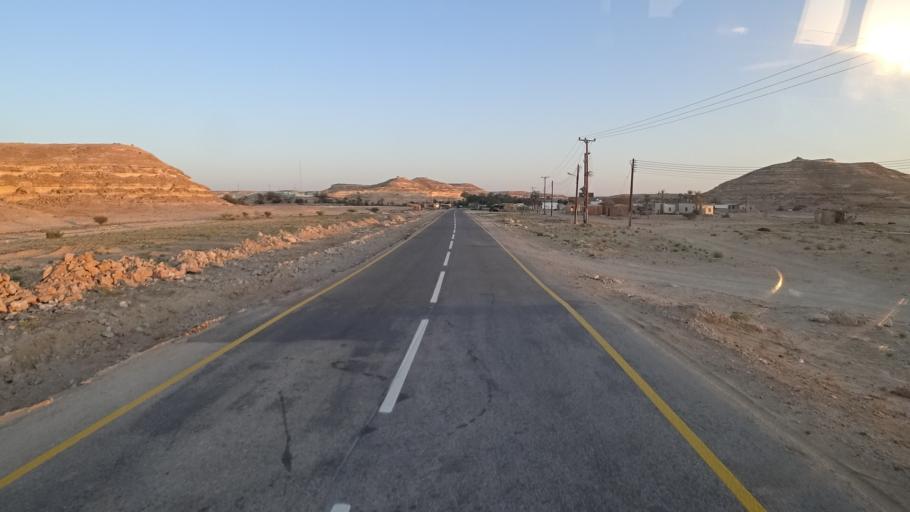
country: OM
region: Zufar
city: Salalah
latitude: 17.4824
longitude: 53.3495
